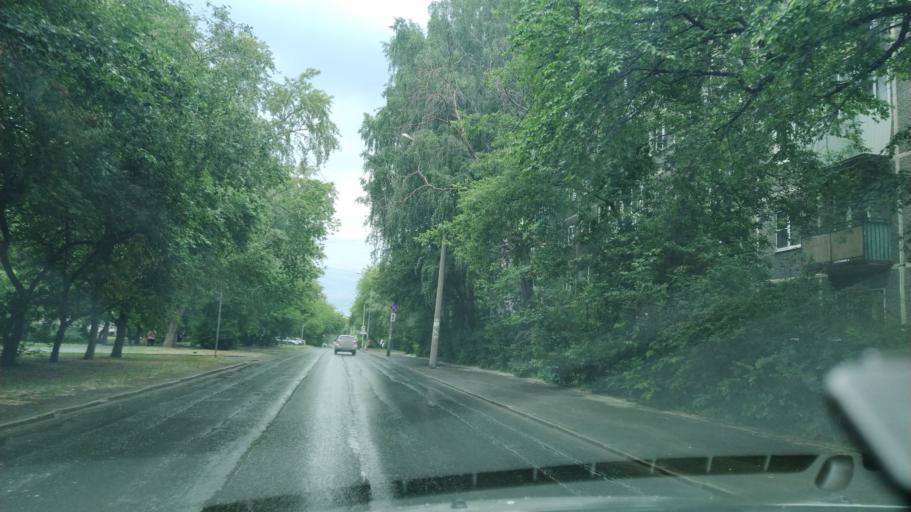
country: RU
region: Sverdlovsk
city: Yekaterinburg
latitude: 56.8306
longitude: 60.6299
